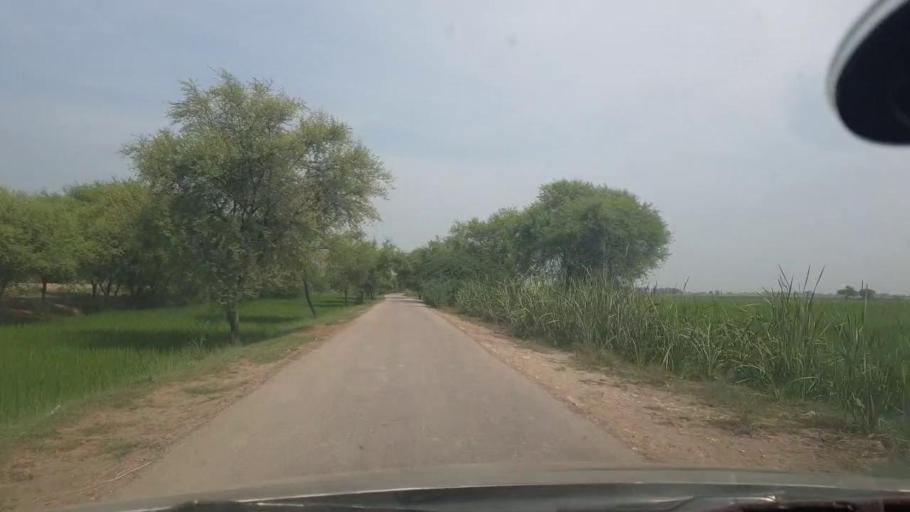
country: PK
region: Sindh
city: Jacobabad
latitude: 28.3001
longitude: 68.4757
